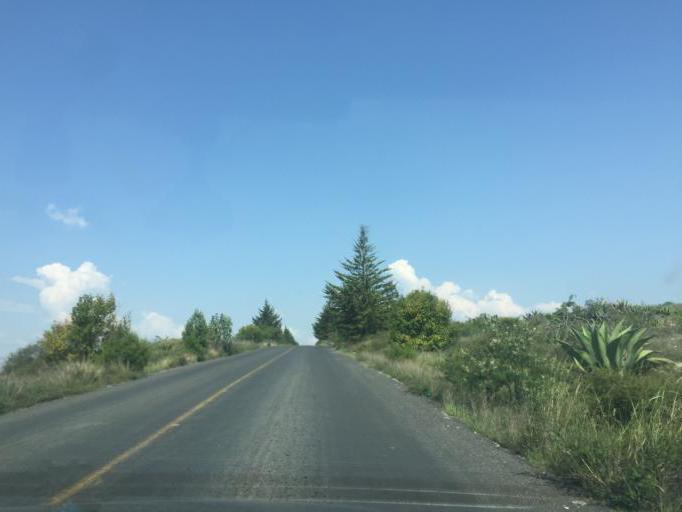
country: MX
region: Hidalgo
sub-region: Cardonal
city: Pozuelos
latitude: 20.6160
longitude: -99.0638
